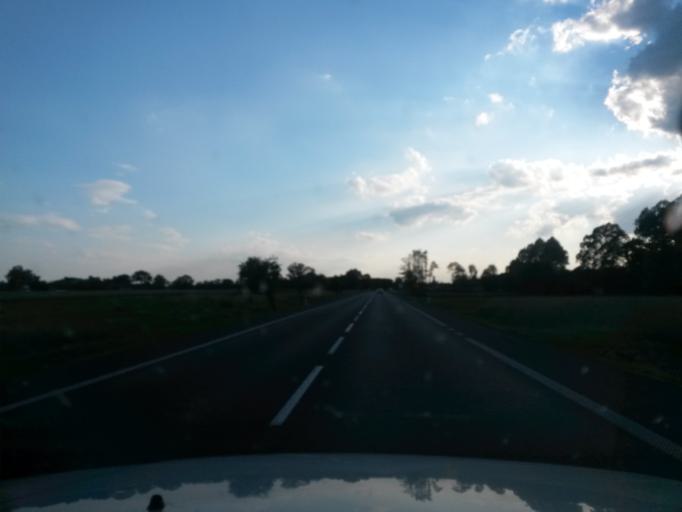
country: PL
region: Lodz Voivodeship
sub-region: Powiat belchatowski
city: Rusiec
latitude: 51.3173
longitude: 18.9551
